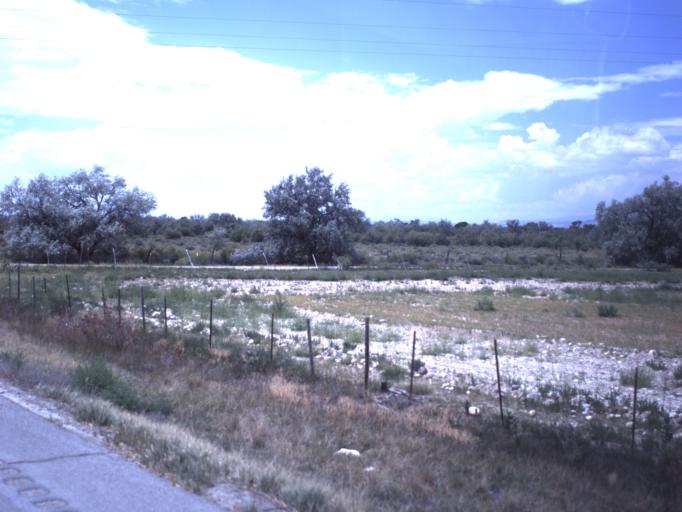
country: US
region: Utah
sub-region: Duchesne County
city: Roosevelt
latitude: 40.1829
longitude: -110.1041
